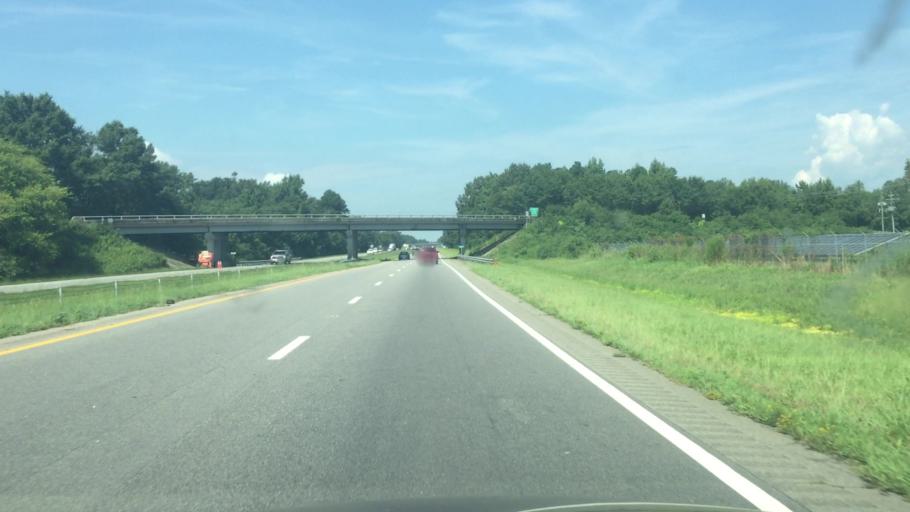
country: US
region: North Carolina
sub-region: Scotland County
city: Laurinburg
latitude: 34.7553
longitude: -79.4443
